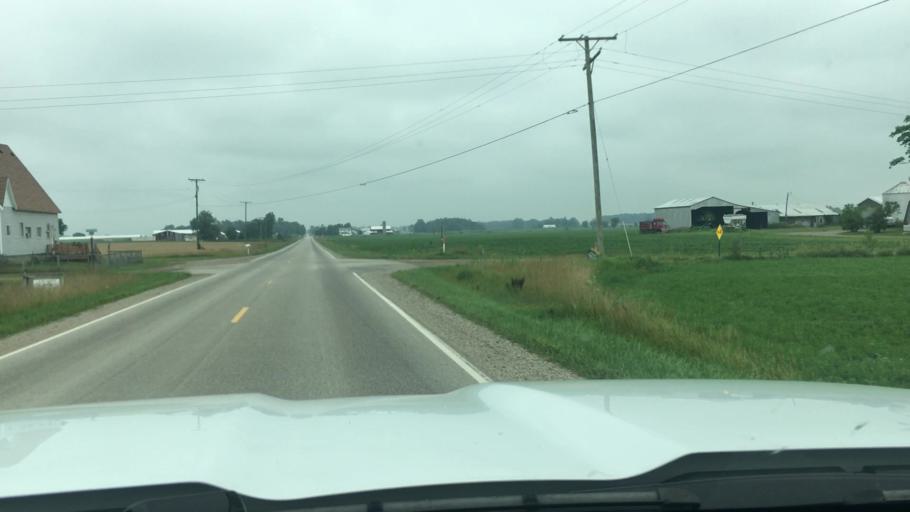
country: US
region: Michigan
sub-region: Sanilac County
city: Brown City
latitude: 43.2849
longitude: -82.9826
